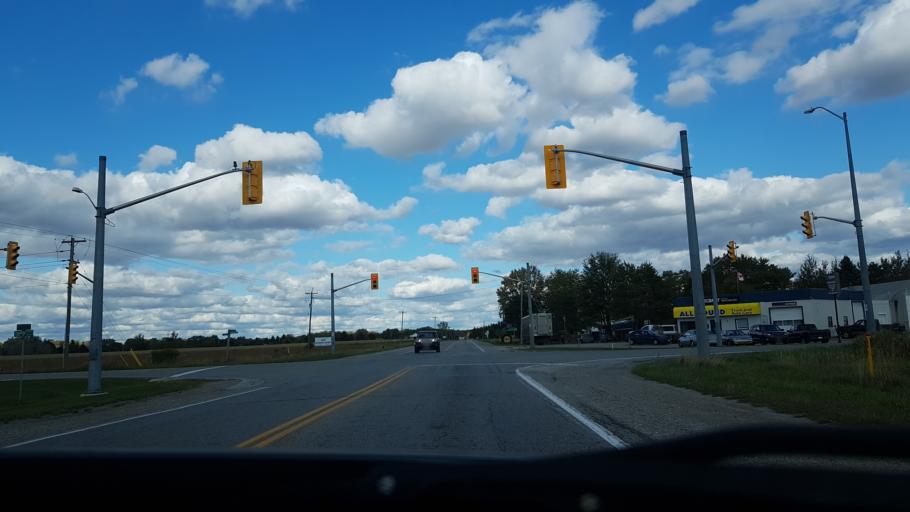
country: CA
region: Ontario
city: South Huron
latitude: 43.1021
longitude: -81.5612
